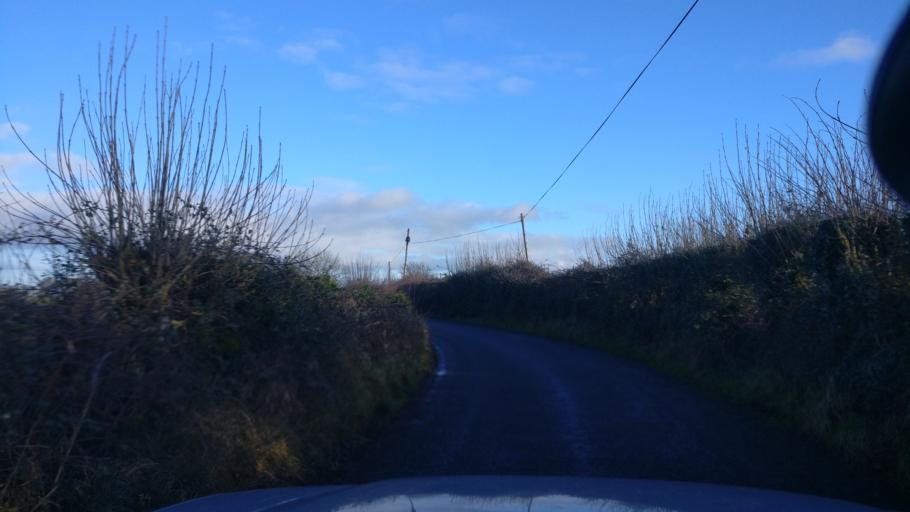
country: IE
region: Connaught
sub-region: County Galway
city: Loughrea
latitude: 53.2287
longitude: -8.5668
